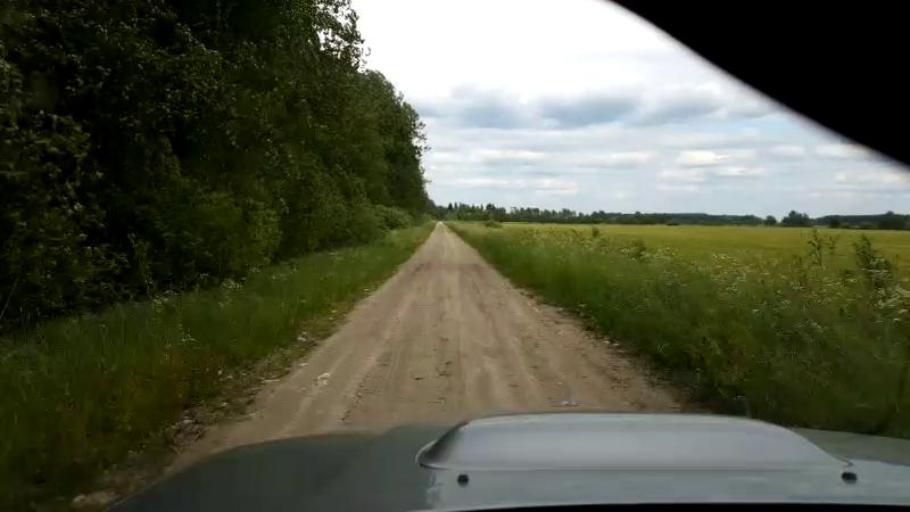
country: EE
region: Paernumaa
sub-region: Sauga vald
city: Sauga
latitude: 58.4955
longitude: 24.5814
